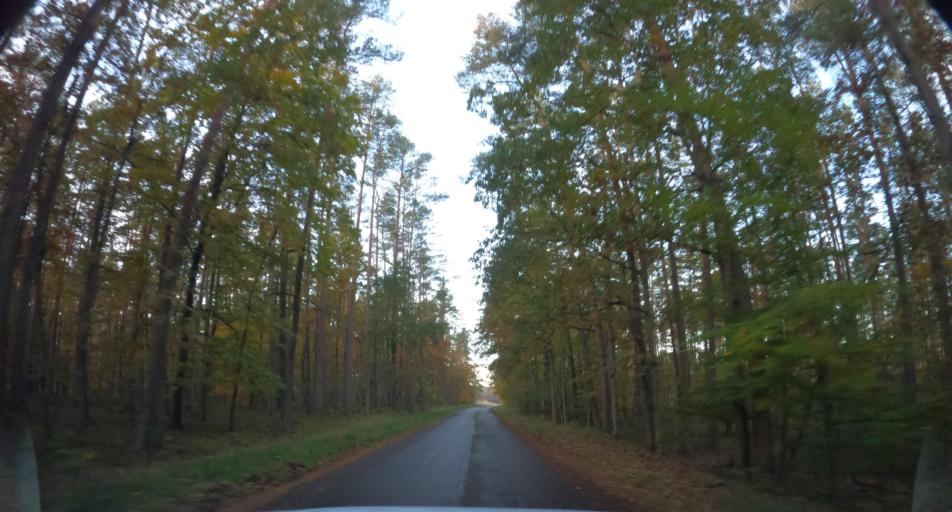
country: PL
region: West Pomeranian Voivodeship
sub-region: Powiat policki
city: Police
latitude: 53.6523
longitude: 14.4672
